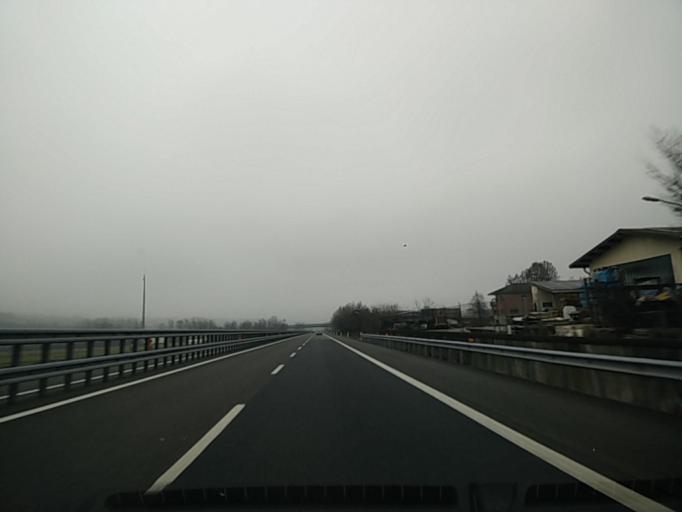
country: IT
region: Piedmont
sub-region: Provincia di Asti
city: Villafranca d'Asti
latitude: 44.9185
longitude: 8.0296
